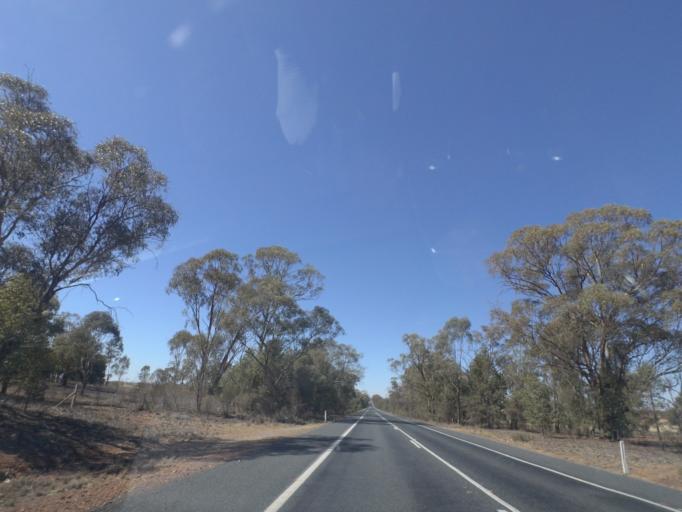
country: AU
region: New South Wales
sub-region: Bland
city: West Wyalong
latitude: -34.1683
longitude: 147.1155
